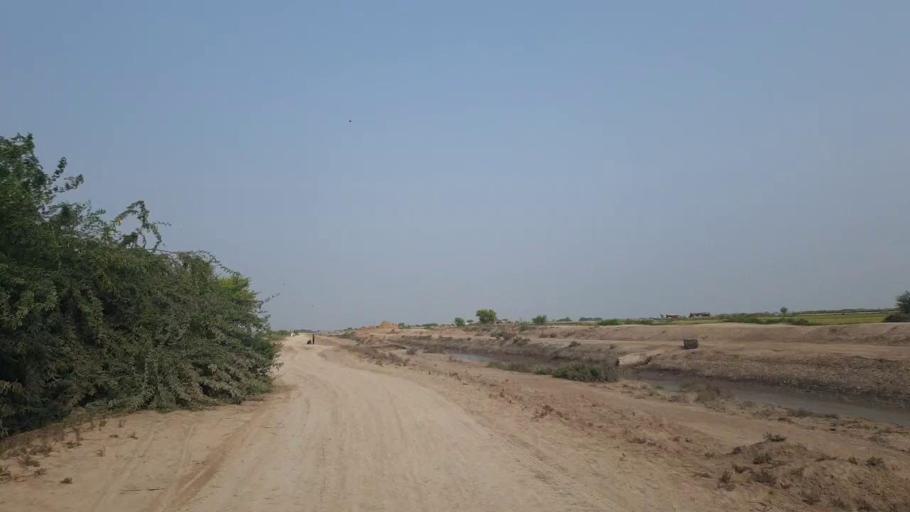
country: PK
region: Sindh
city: Badin
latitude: 24.7079
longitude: 68.7742
